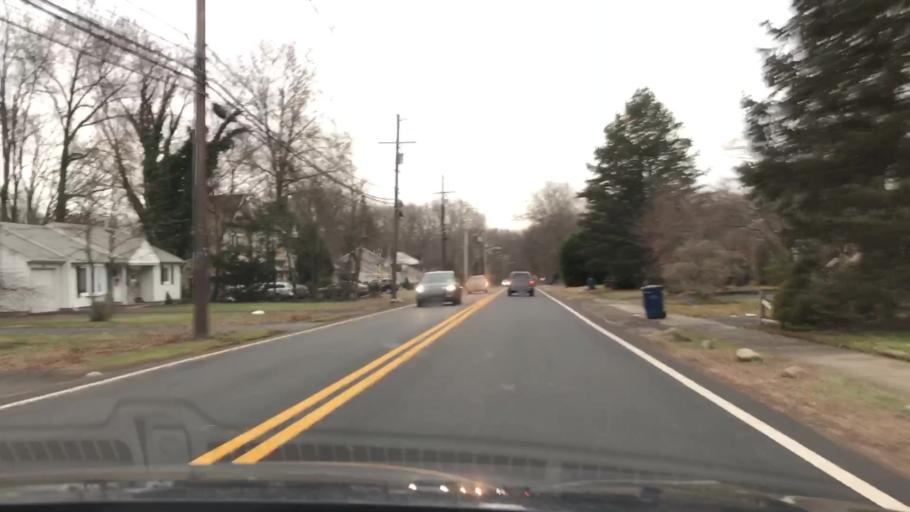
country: US
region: New Jersey
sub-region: Bergen County
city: Norwood
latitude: 40.9909
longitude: -73.9577
